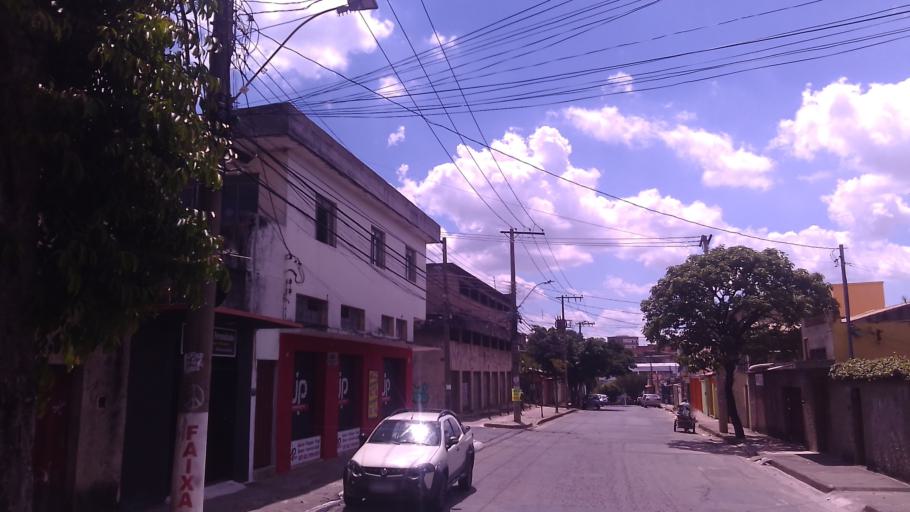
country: BR
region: Minas Gerais
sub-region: Contagem
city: Contagem
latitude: -19.9014
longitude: -44.0080
